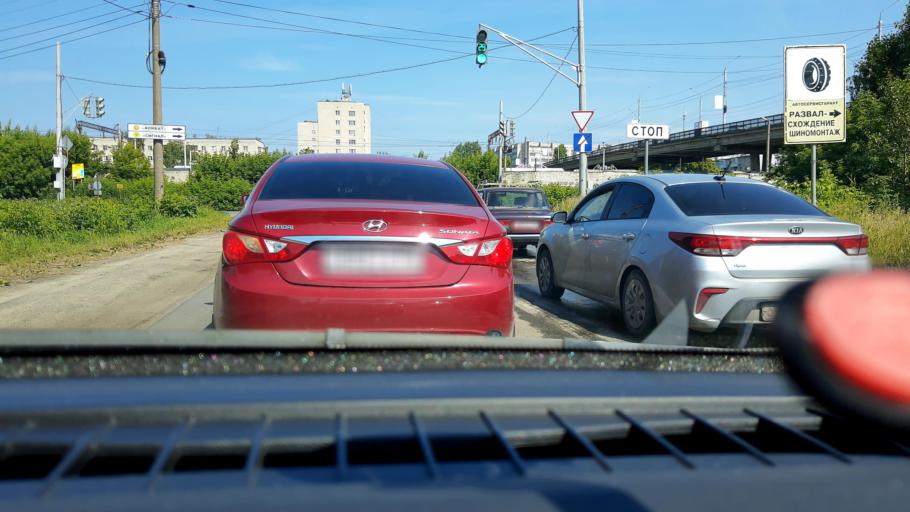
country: RU
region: Nizjnij Novgorod
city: Dzerzhinsk
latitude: 56.2337
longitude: 43.4890
